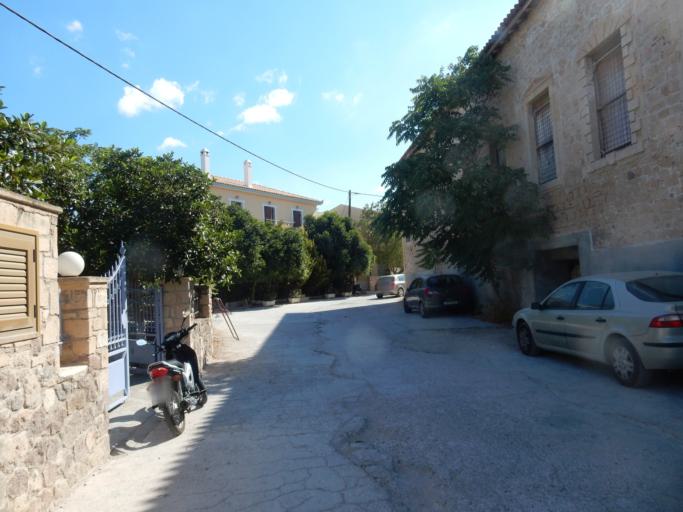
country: GR
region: Attica
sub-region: Nomos Piraios
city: Aegina
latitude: 37.7438
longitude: 23.4333
